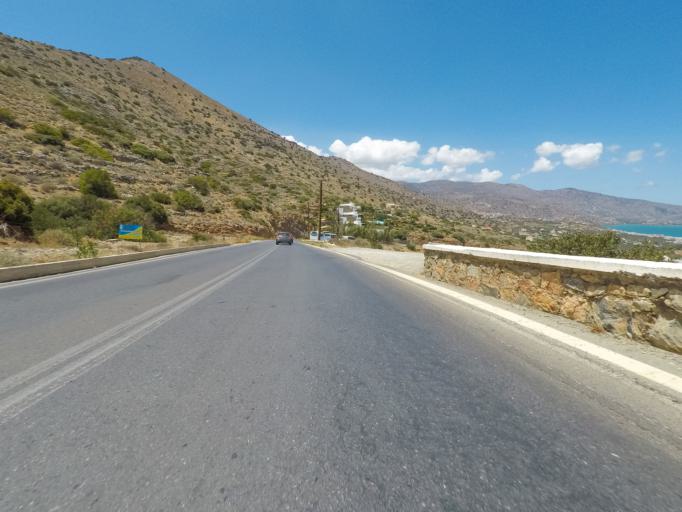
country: GR
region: Crete
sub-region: Nomos Lasithiou
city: Skhisma
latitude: 35.2375
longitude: 25.7282
